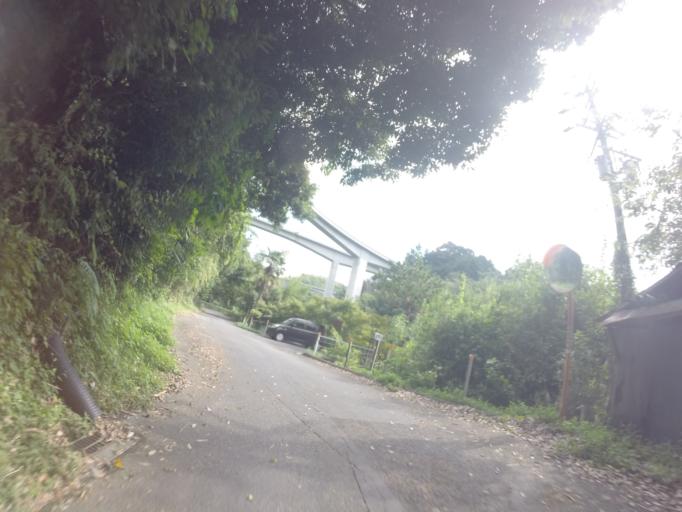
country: JP
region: Shizuoka
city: Shizuoka-shi
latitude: 35.0750
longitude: 138.4618
